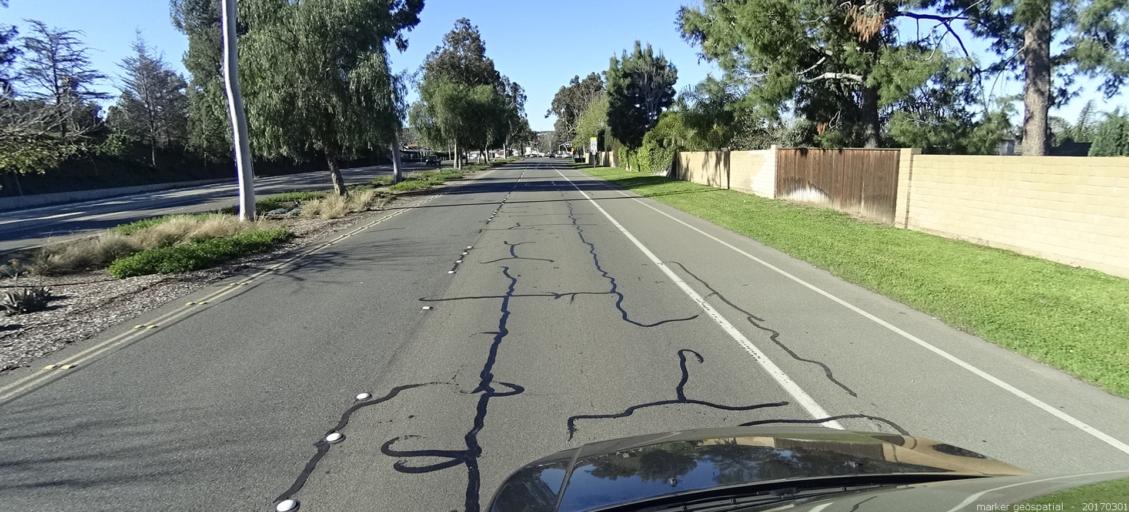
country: US
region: California
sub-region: Orange County
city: Yorba Linda
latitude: 33.8591
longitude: -117.7690
